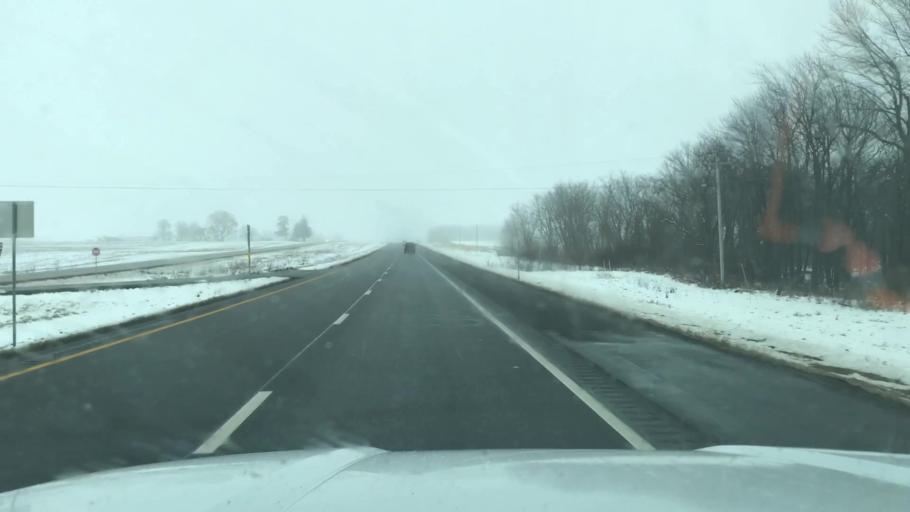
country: US
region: Missouri
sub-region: DeKalb County
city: Maysville
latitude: 39.7614
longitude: -94.3944
